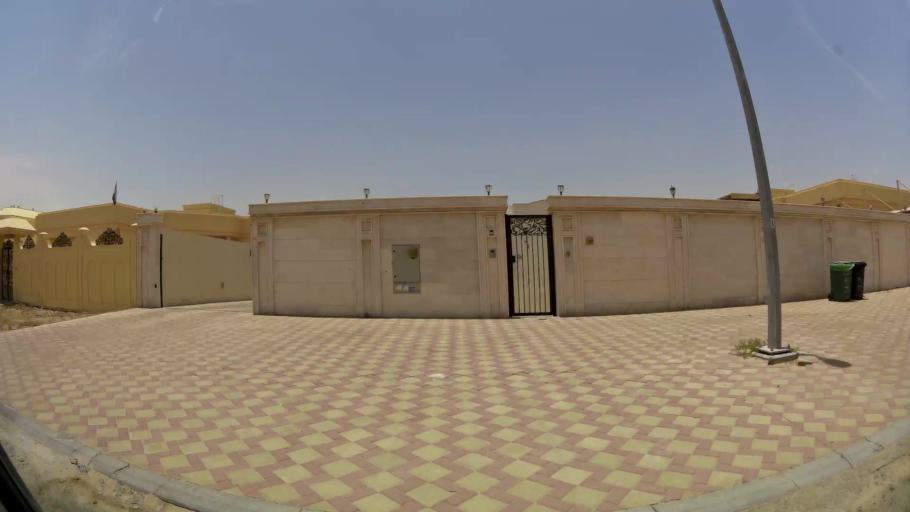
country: AE
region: Ash Shariqah
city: Sharjah
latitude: 25.2334
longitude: 55.4584
